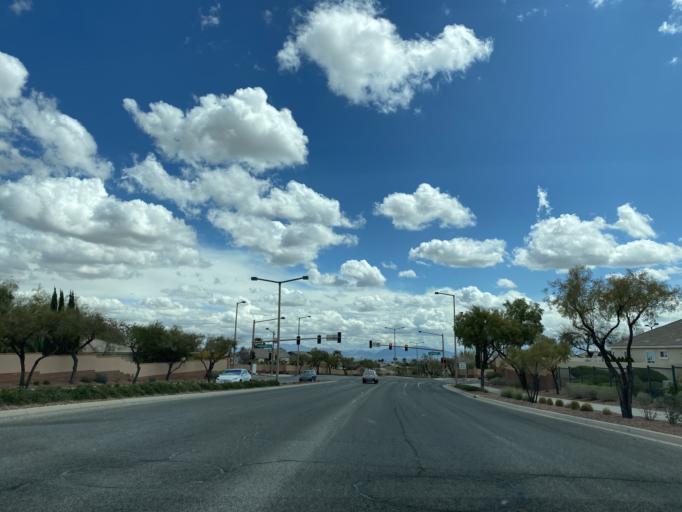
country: US
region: Nevada
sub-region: Clark County
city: Summerlin South
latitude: 36.1854
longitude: -115.3304
